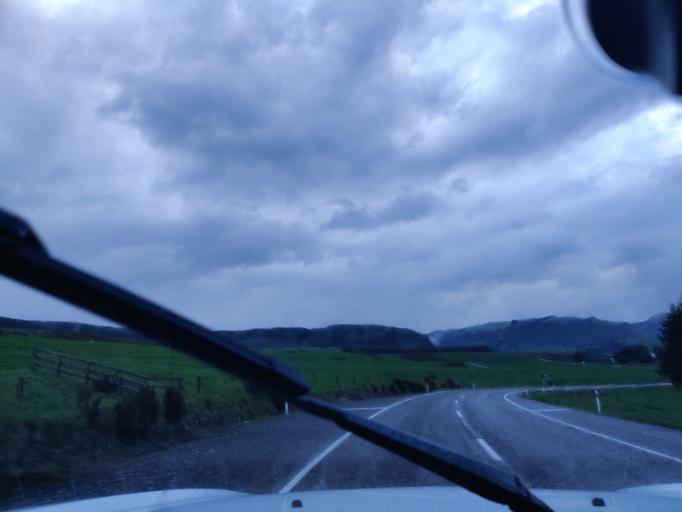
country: NZ
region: Waikato
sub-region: South Waikato District
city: Tokoroa
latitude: -38.4157
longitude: 175.8100
